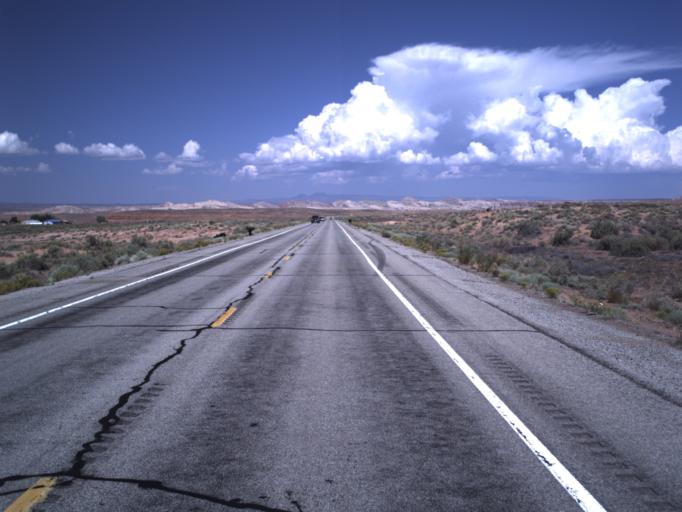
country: US
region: Utah
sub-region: San Juan County
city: Blanding
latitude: 37.2079
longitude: -109.6087
